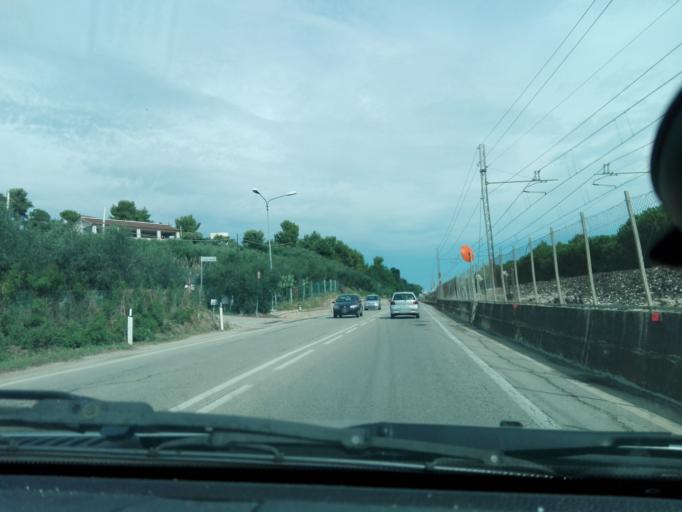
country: IT
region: Abruzzo
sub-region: Provincia di Teramo
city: Pineto
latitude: 42.5868
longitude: 14.0867
